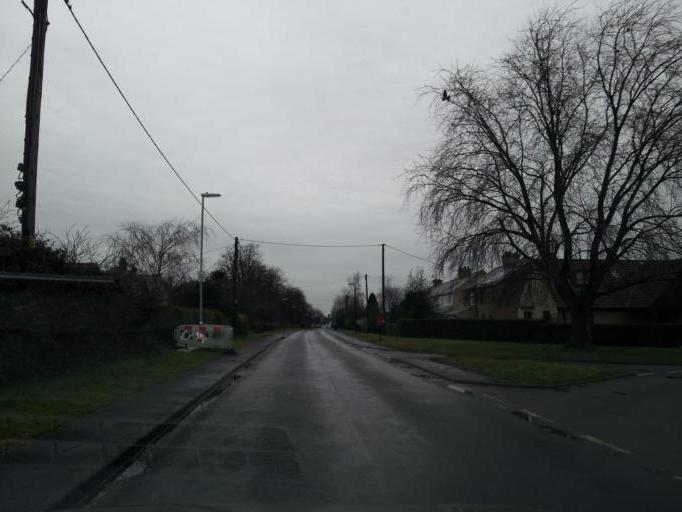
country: GB
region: England
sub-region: Cambridgeshire
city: Bottisham
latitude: 52.2377
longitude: 0.2477
